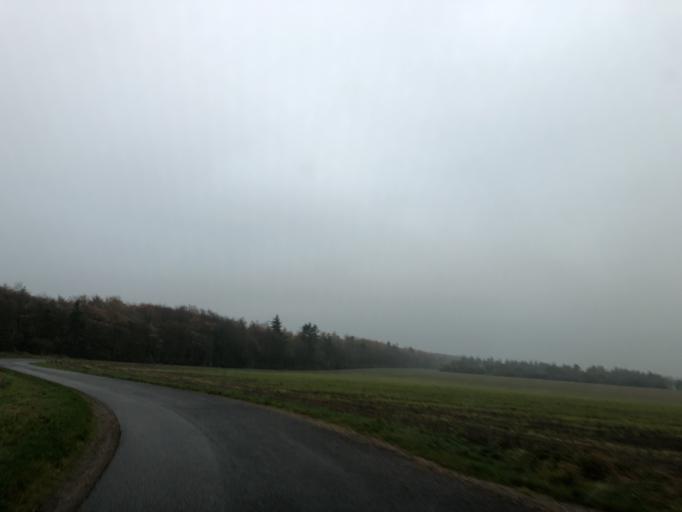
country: DK
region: Central Jutland
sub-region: Herning Kommune
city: Vildbjerg
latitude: 56.2017
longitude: 8.6713
